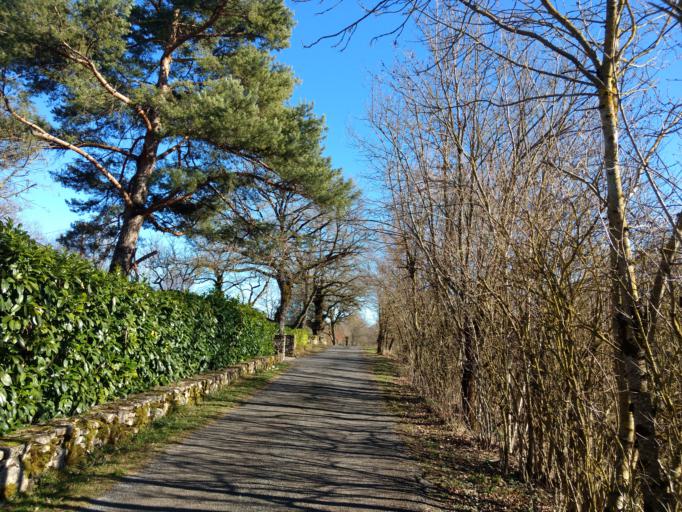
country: FR
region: Midi-Pyrenees
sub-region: Departement de l'Aveyron
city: Sebazac-Concoures
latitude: 44.4177
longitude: 2.5679
